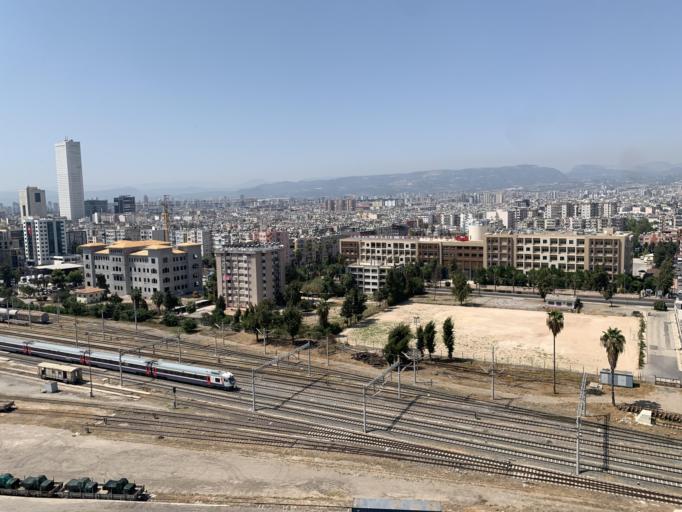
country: TR
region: Mersin
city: Mercin
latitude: 36.8040
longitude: 34.6374
